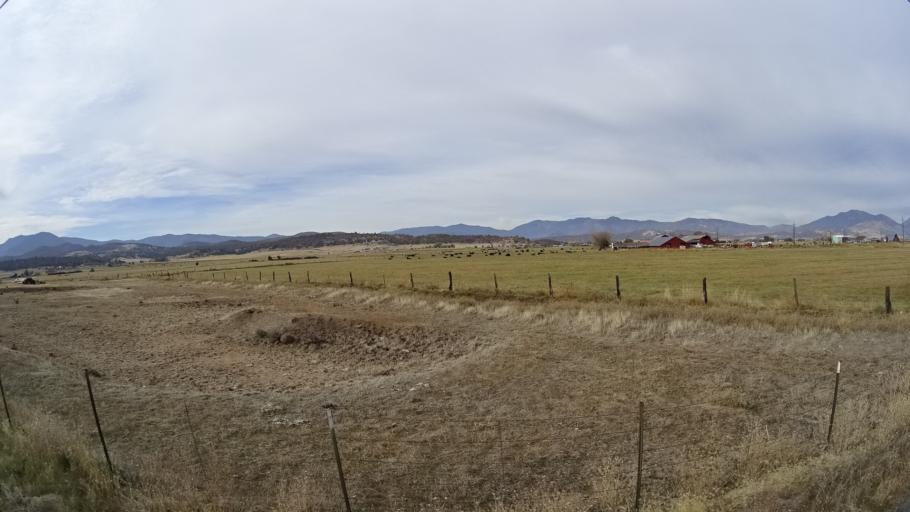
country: US
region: California
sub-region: Siskiyou County
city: Montague
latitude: 41.7038
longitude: -122.5494
